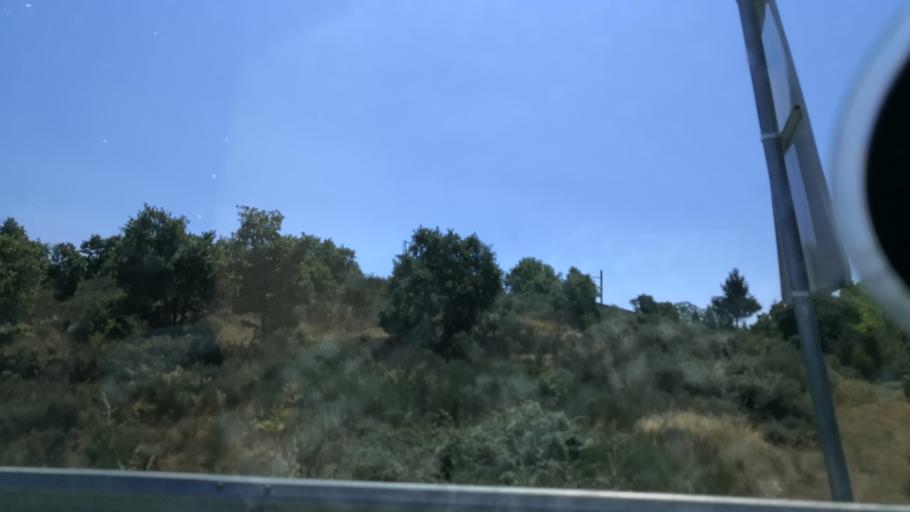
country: PT
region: Braganca
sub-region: Braganca Municipality
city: Braganca
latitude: 41.7693
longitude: -6.7920
